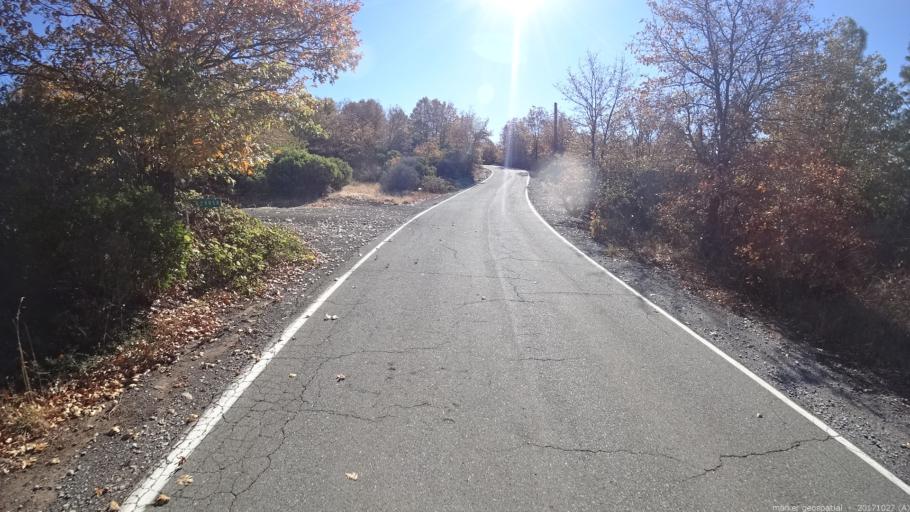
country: US
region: California
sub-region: Shasta County
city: Burney
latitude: 40.7923
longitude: -121.9323
